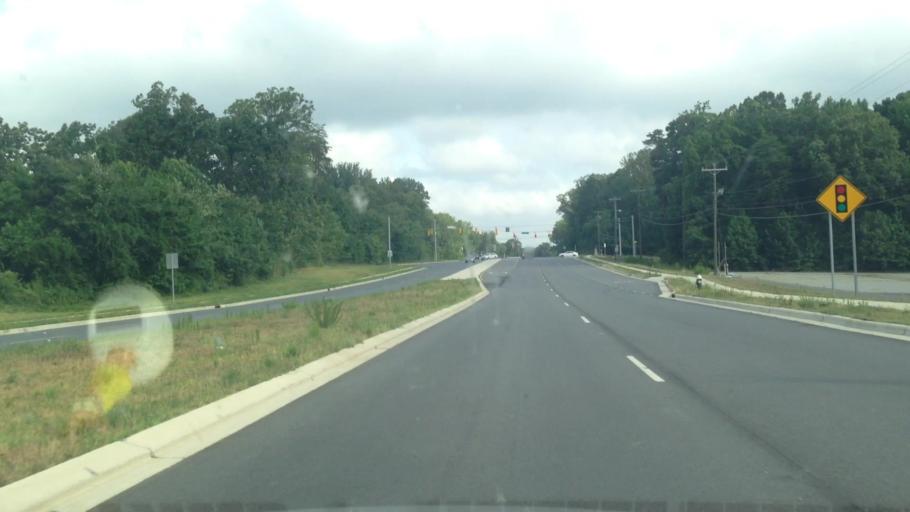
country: US
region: North Carolina
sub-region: Guilford County
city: Summerfield
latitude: 36.1585
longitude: -79.8748
